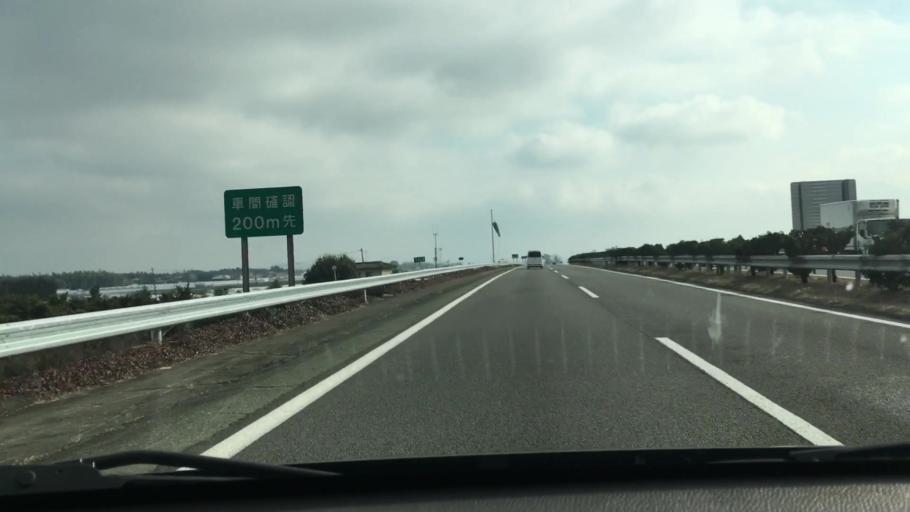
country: JP
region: Kumamoto
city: Ueki
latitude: 32.8889
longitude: 130.7228
